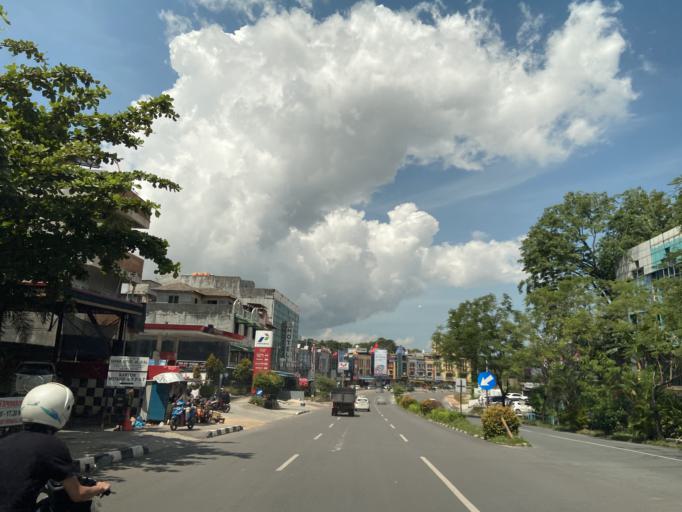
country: SG
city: Singapore
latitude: 1.1346
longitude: 104.0172
